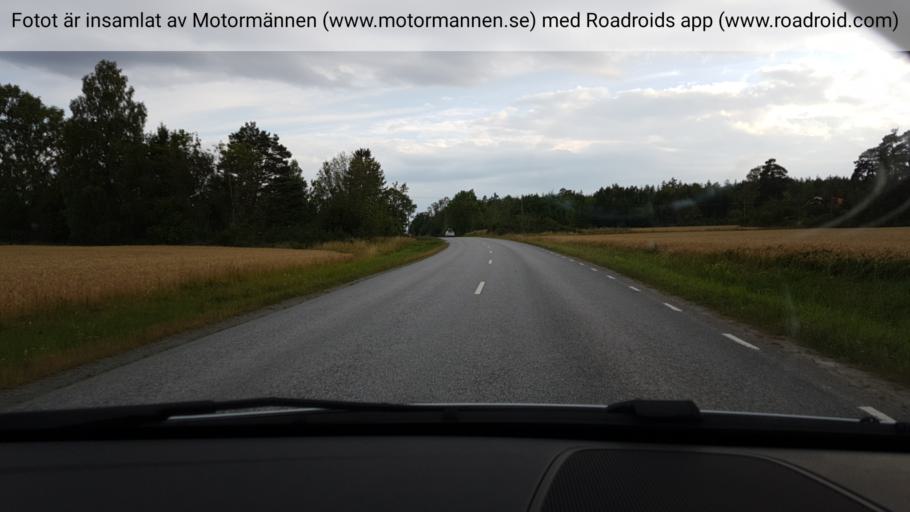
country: SE
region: Uppsala
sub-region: Uppsala Kommun
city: Alsike
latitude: 59.6933
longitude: 17.7153
